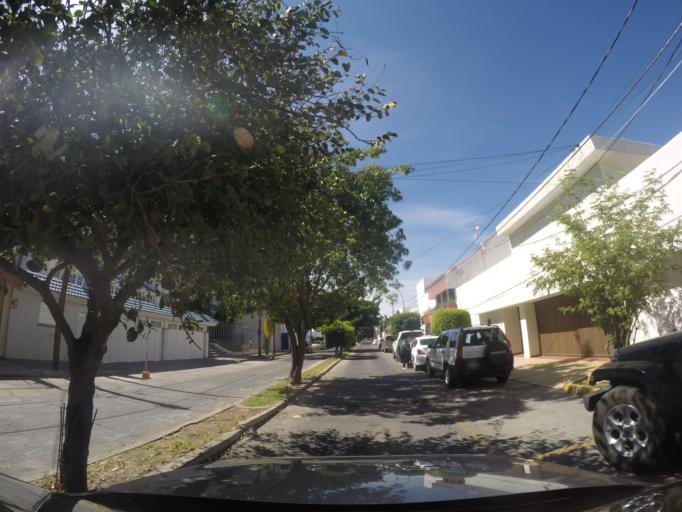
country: MX
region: San Luis Potosi
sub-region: San Luis Potosi
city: San Luis Potosi
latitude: 22.1494
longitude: -101.0107
